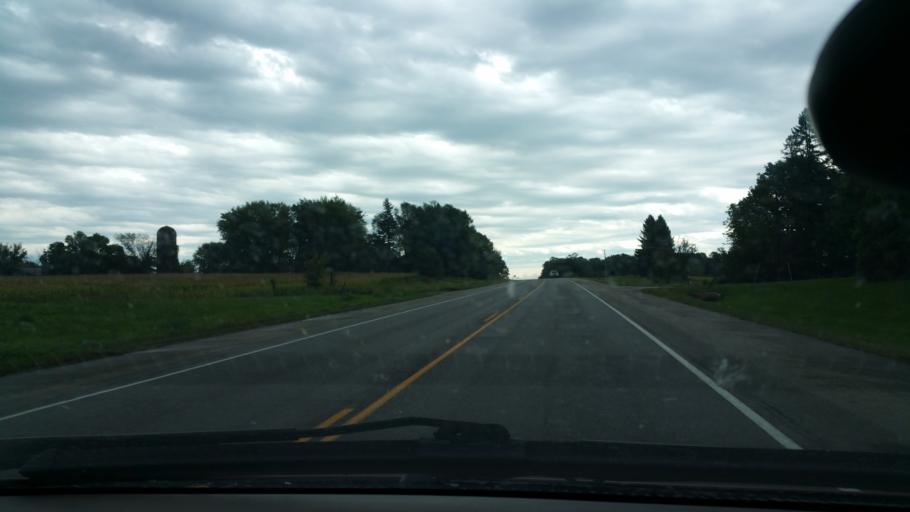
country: US
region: Minnesota
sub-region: Rice County
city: Dundas
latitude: 44.4718
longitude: -93.2753
